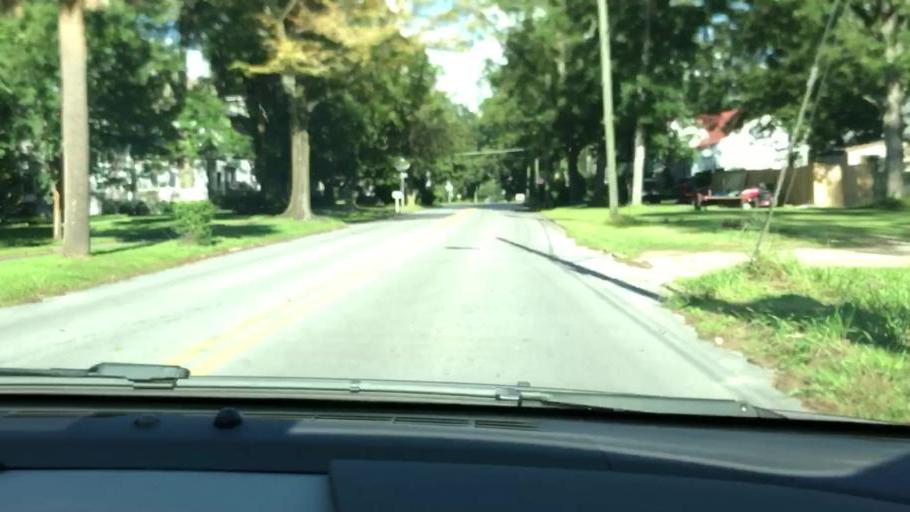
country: US
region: Florida
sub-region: Washington County
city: Chipley
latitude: 30.7862
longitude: -85.5414
